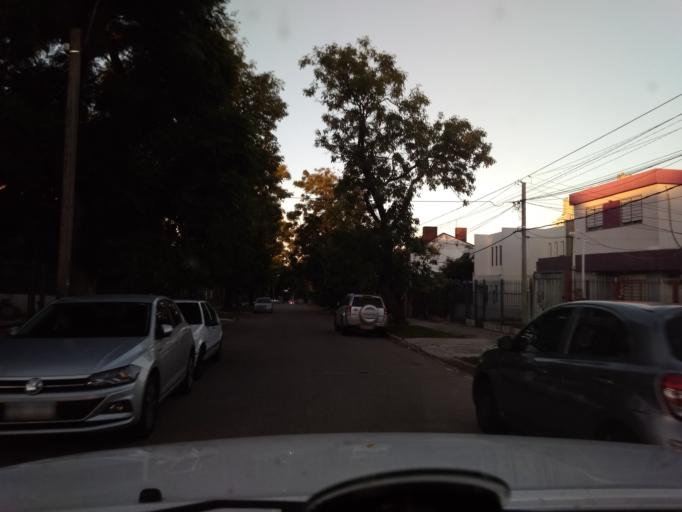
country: UY
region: Montevideo
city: Montevideo
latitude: -34.8956
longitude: -56.1251
